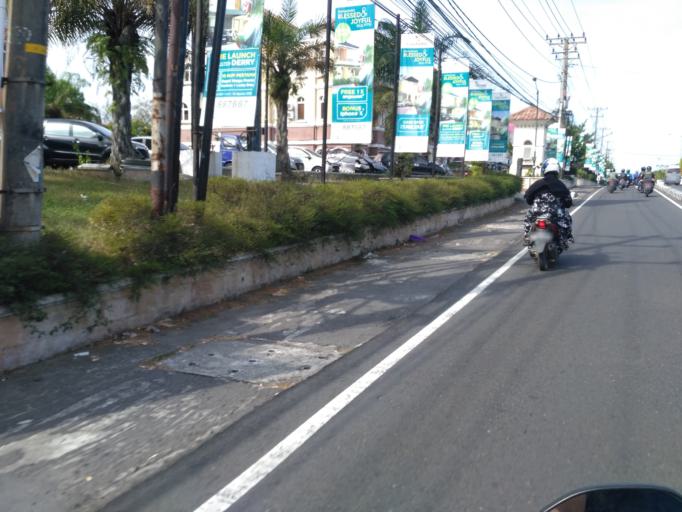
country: ID
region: Daerah Istimewa Yogyakarta
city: Depok
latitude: -7.7632
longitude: 110.4192
